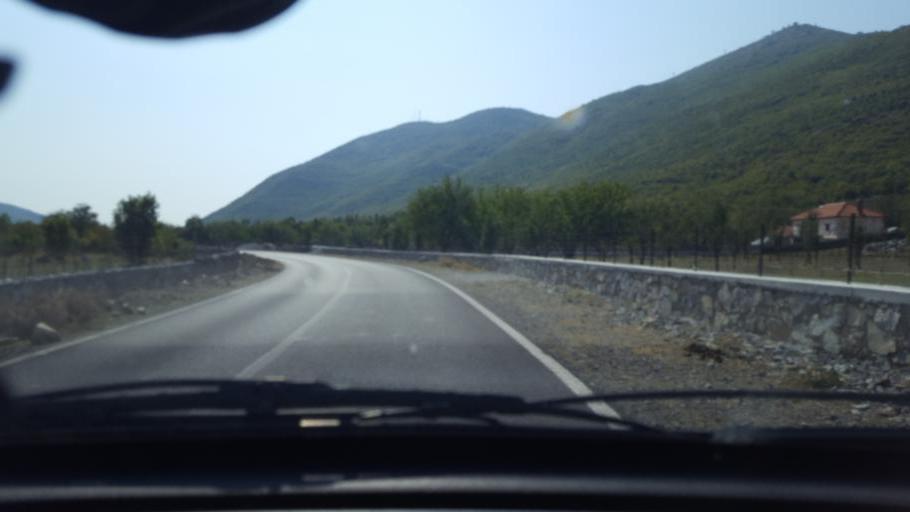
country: AL
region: Shkoder
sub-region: Rrethi i Malesia e Madhe
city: Kastrat
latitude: 42.4050
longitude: 19.4965
